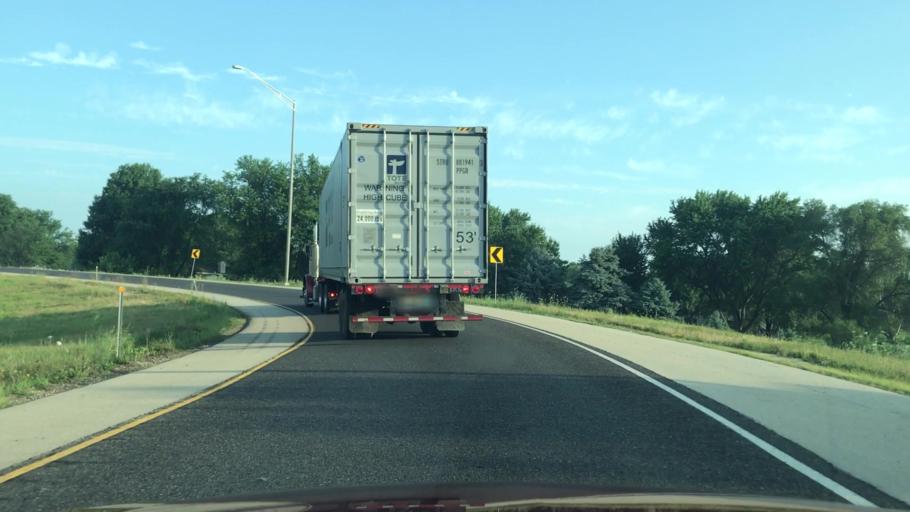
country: US
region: Illinois
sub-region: Winnebago County
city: Cherry Valley
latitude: 42.2491
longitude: -88.9587
